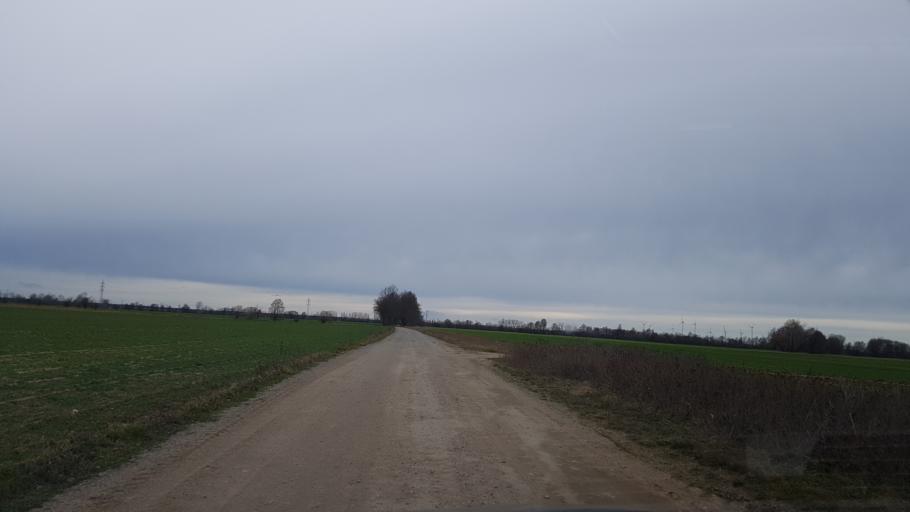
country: DE
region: Brandenburg
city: Bad Liebenwerda
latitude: 51.4901
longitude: 13.3820
